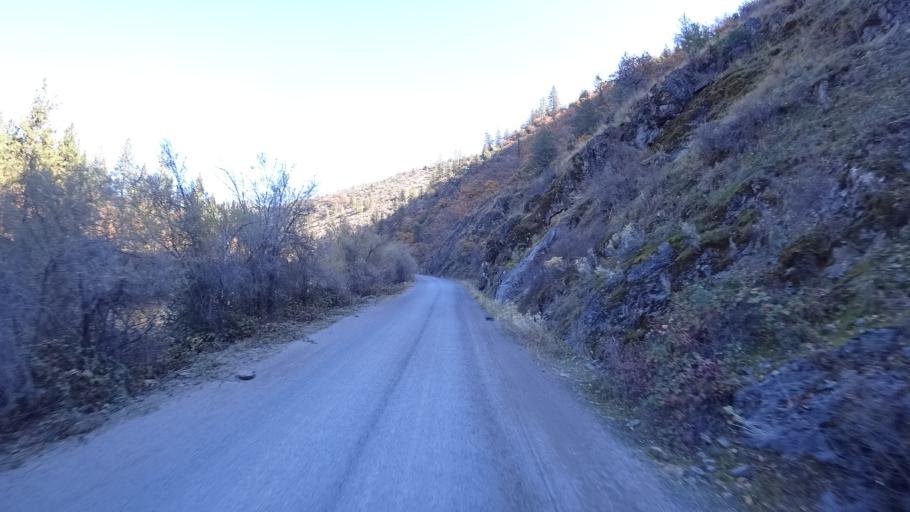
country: US
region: California
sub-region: Siskiyou County
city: Yreka
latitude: 41.8271
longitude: -122.6442
